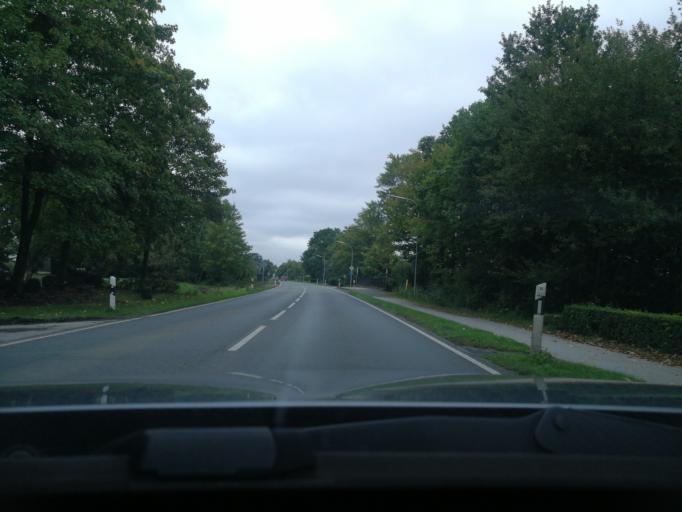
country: DE
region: North Rhine-Westphalia
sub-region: Regierungsbezirk Dusseldorf
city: Kevelaer
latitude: 51.5393
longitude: 6.2467
